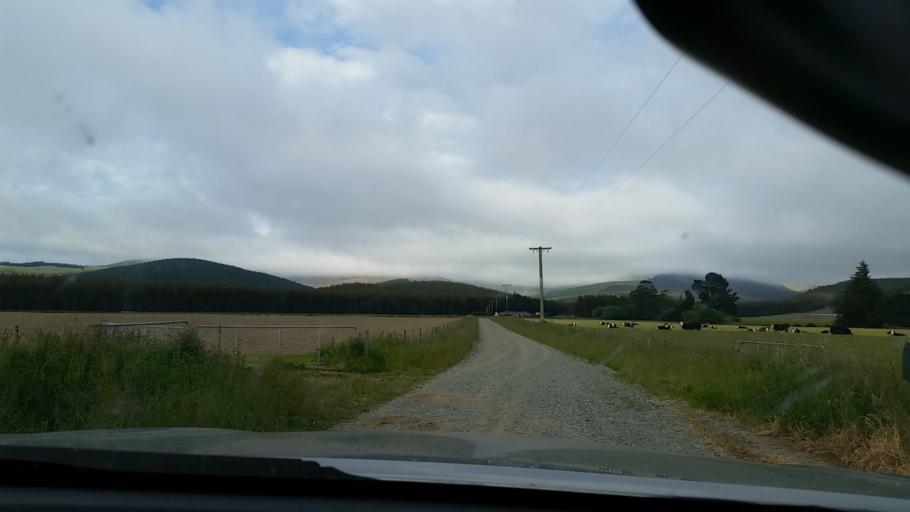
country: NZ
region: Southland
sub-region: Southland District
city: Winton
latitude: -45.9097
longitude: 168.2802
